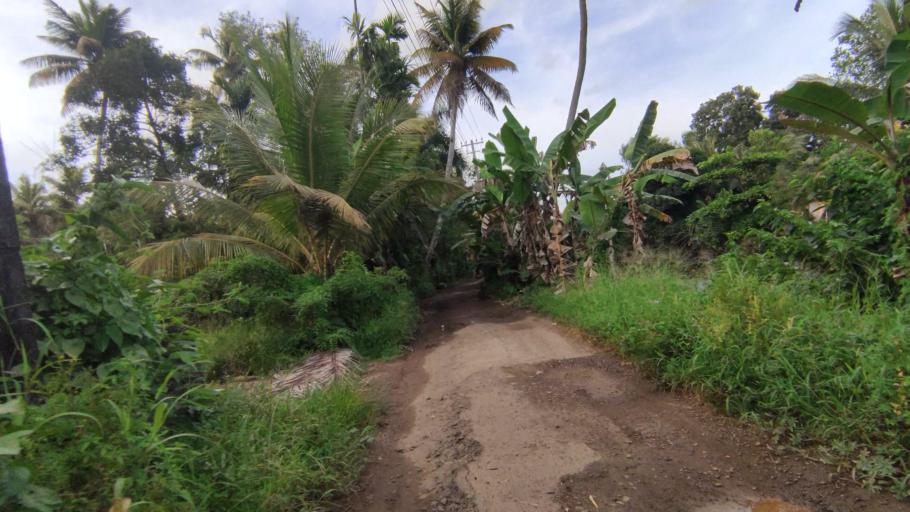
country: IN
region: Kerala
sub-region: Kottayam
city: Kottayam
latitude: 9.6023
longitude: 76.4398
